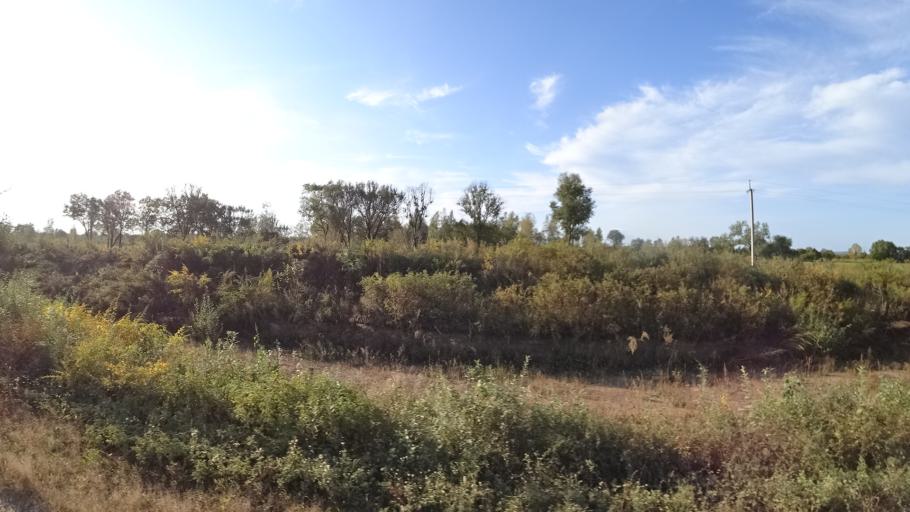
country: RU
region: Amur
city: Arkhara
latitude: 49.3514
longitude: 130.1318
